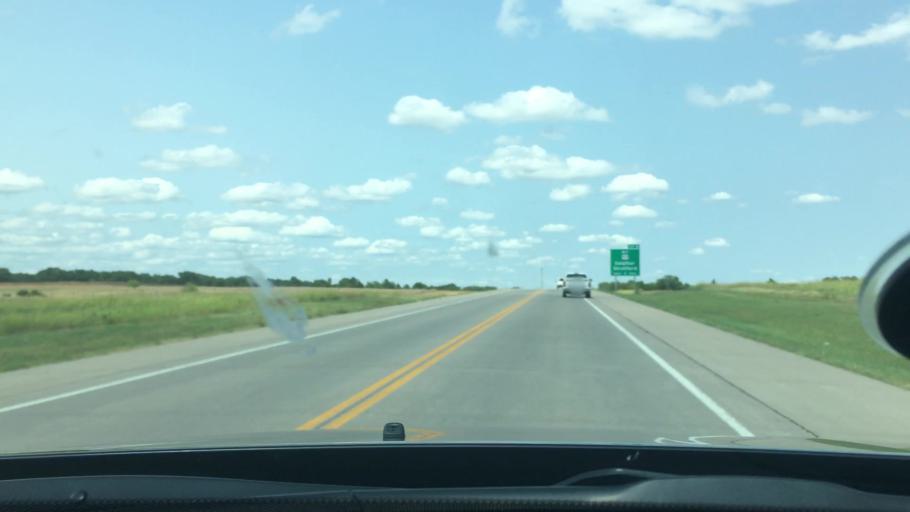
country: US
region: Oklahoma
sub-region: Murray County
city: Sulphur
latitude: 34.5367
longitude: -96.9917
